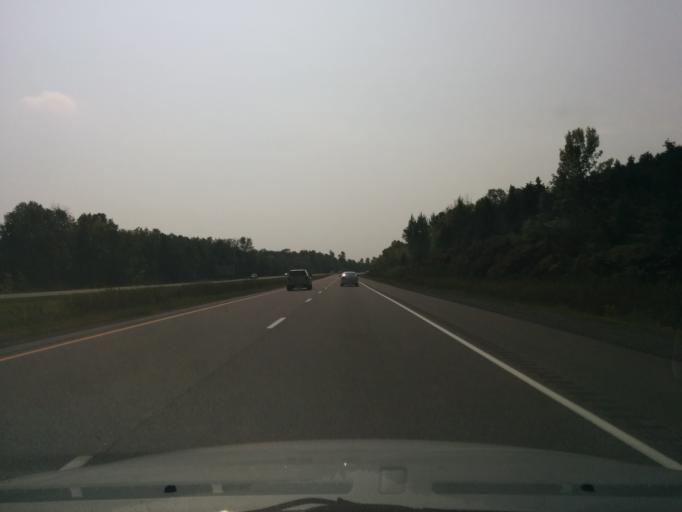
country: CA
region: Ontario
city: Bells Corners
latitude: 45.1360
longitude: -75.6766
